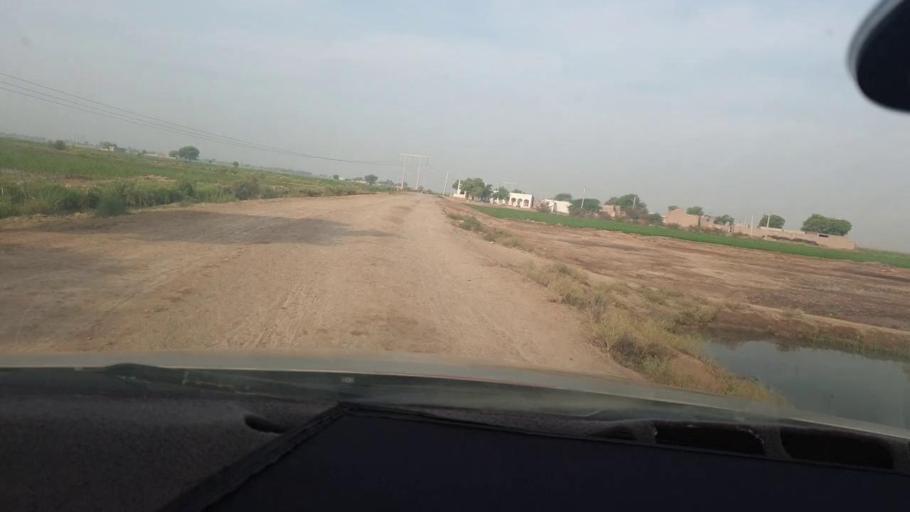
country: PK
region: Sindh
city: Jacobabad
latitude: 28.3355
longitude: 68.4043
